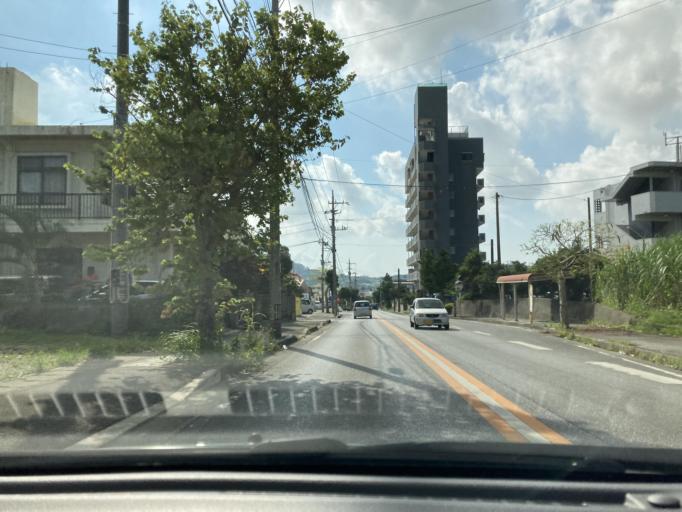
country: JP
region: Okinawa
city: Tomigusuku
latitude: 26.1599
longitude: 127.7456
